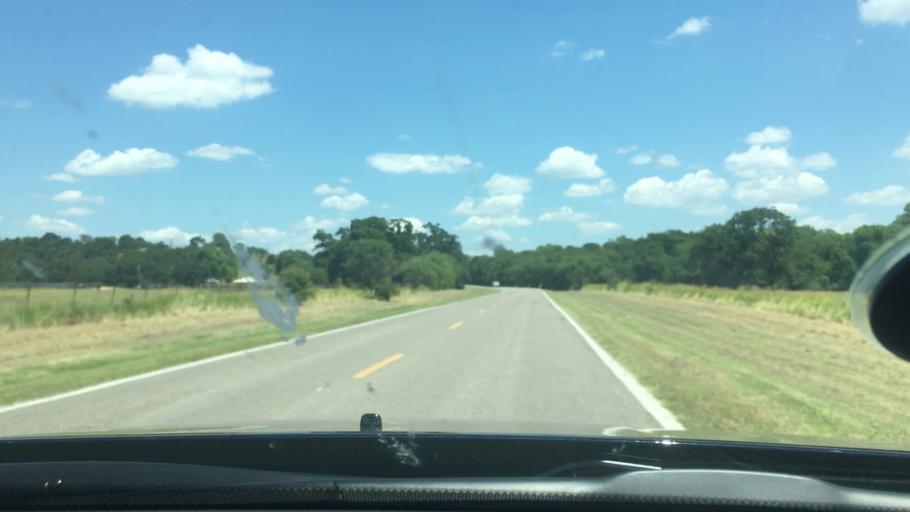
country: US
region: Oklahoma
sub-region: Carter County
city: Dickson
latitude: 34.3041
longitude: -96.9640
